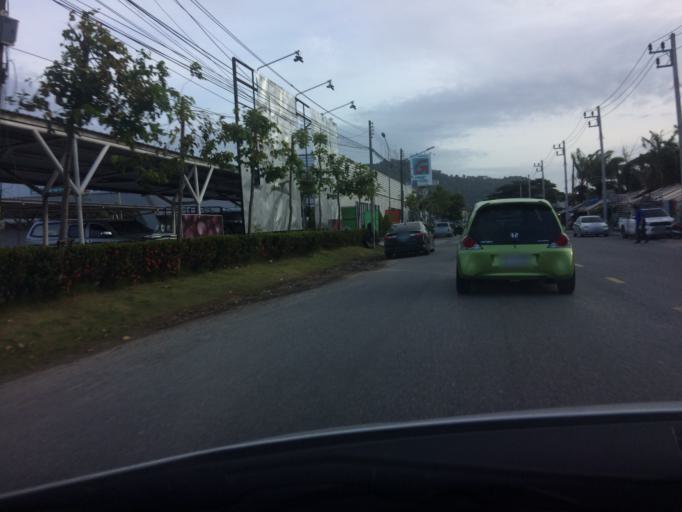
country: TH
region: Phuket
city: Ban Talat Yai
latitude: 7.8769
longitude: 98.3986
